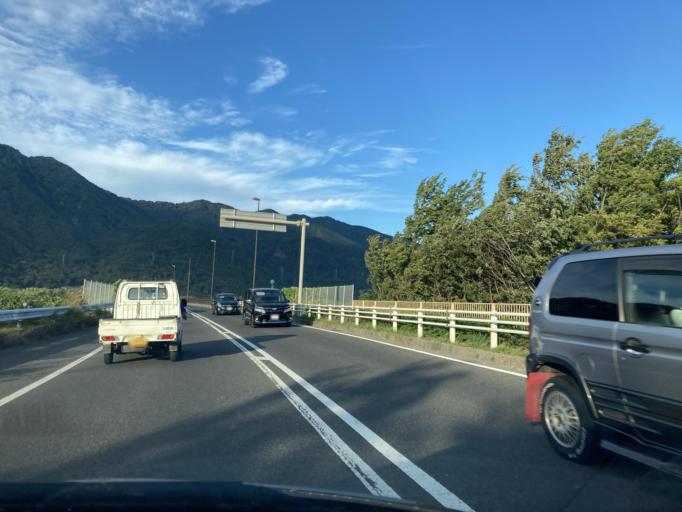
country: JP
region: Nagano
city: Ueda
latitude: 36.4062
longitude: 138.2138
